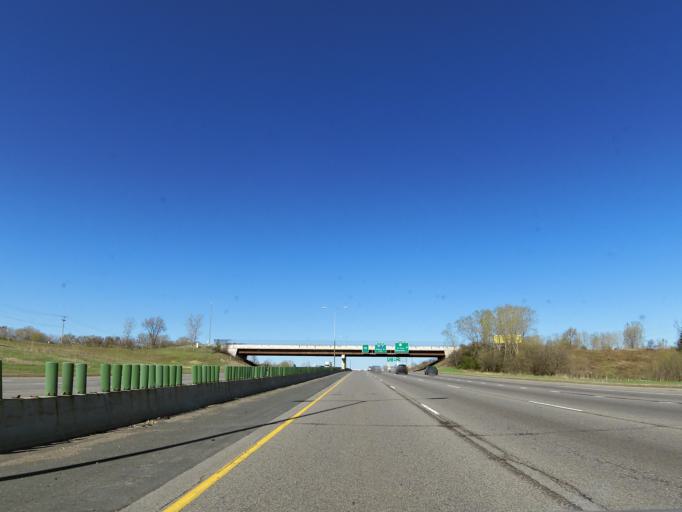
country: US
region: Minnesota
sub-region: Dakota County
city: South Saint Paul
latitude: 44.8748
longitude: -93.0502
